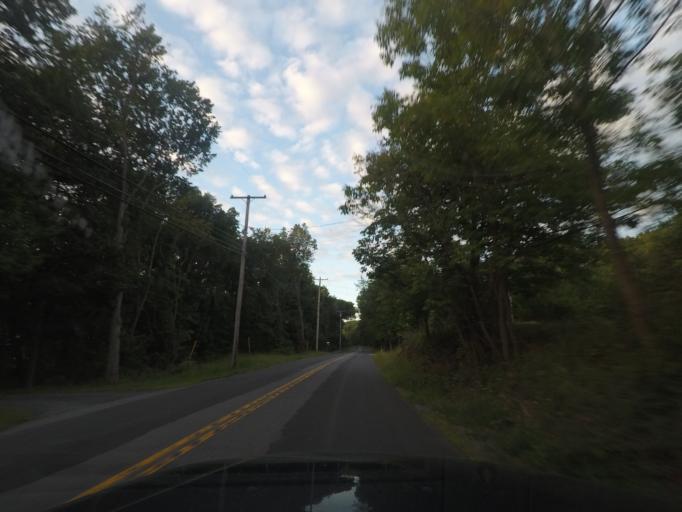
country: US
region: New York
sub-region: Rensselaer County
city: Nassau
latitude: 42.5231
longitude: -73.6049
